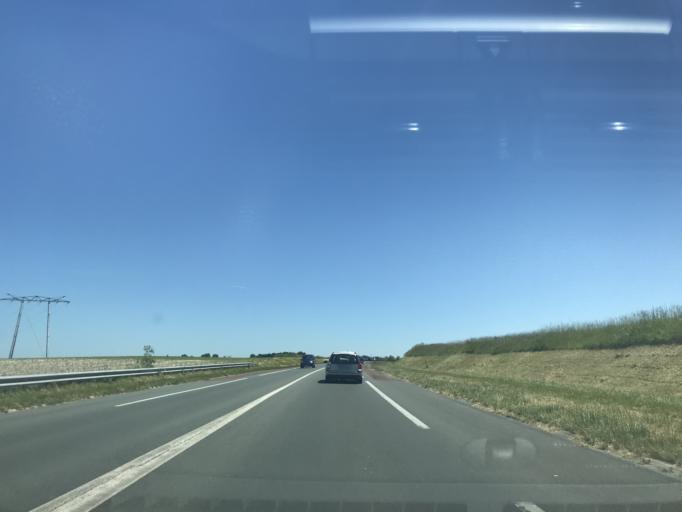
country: FR
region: Poitou-Charentes
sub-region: Departement de la Charente-Maritime
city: Saint-Georges-de-Didonne
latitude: 45.6120
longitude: -0.9813
